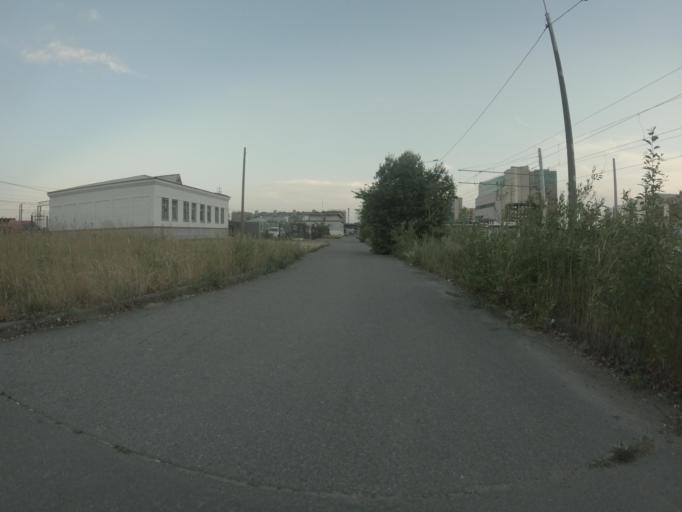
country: RU
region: St.-Petersburg
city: Krasnogvargeisky
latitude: 59.9349
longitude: 30.4440
